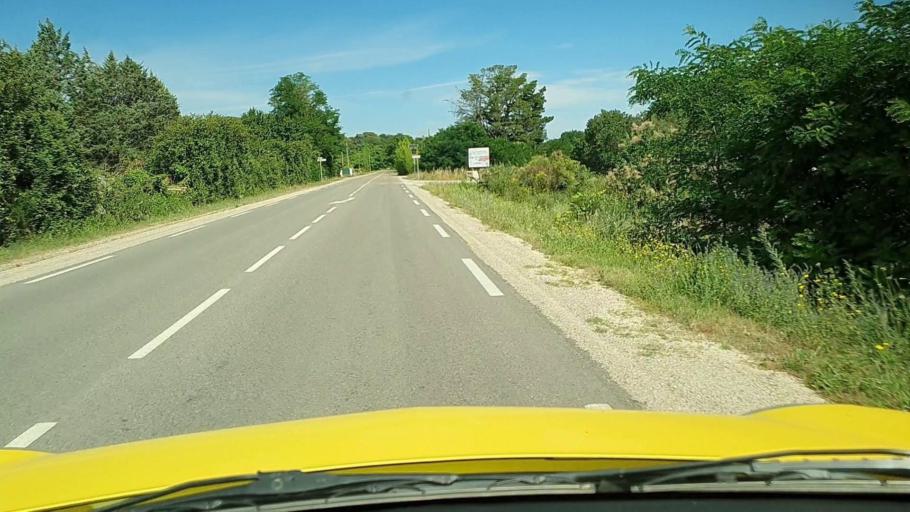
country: FR
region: Languedoc-Roussillon
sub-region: Departement du Gard
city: Moussac
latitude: 43.9855
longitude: 4.1954
